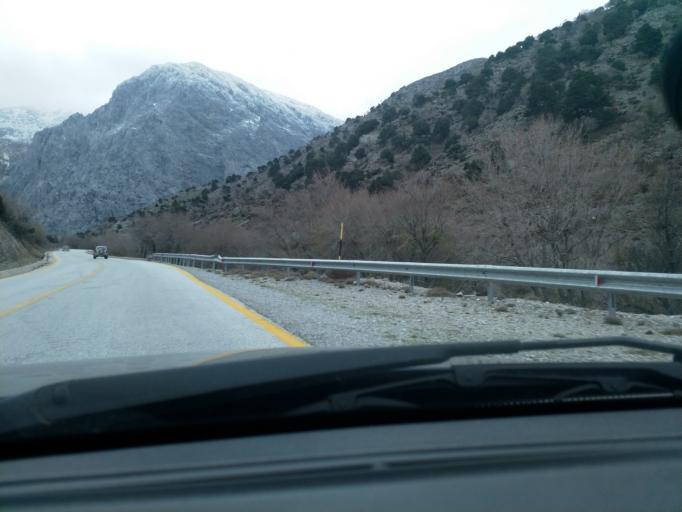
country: GR
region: Crete
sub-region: Nomos Chanias
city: Perivolia
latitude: 35.3133
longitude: 23.9158
